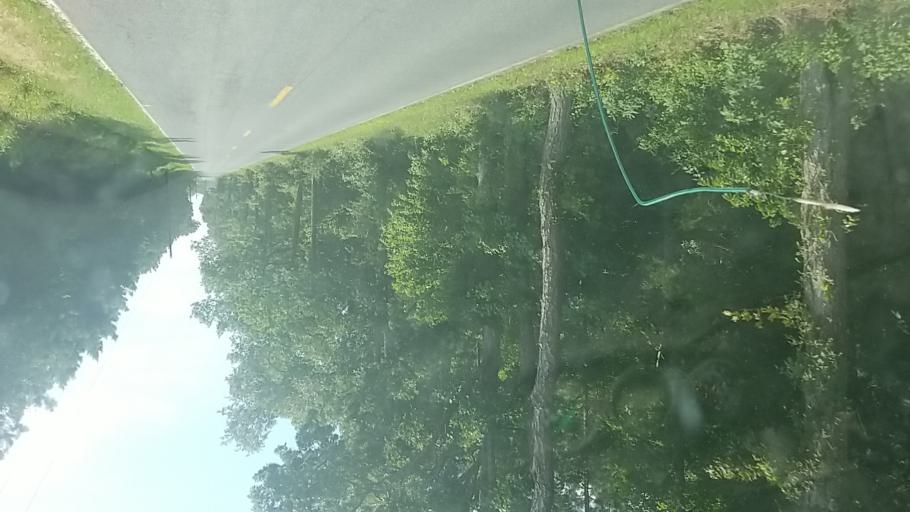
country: US
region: Maryland
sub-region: Wicomico County
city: Hebron
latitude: 38.4371
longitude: -75.6982
